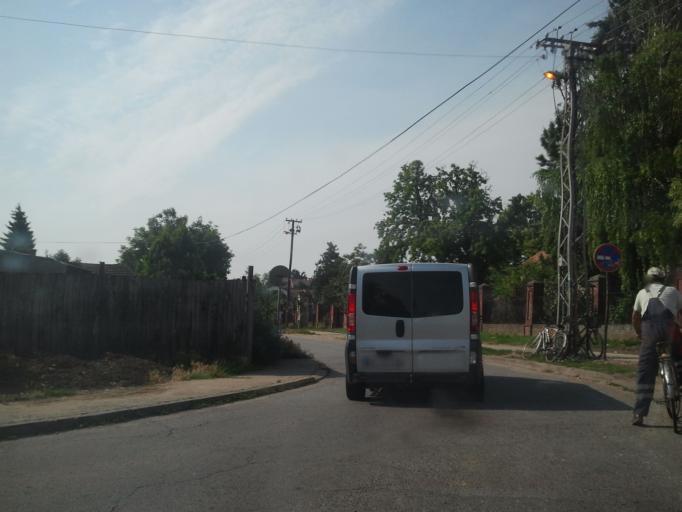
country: RS
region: Autonomna Pokrajina Vojvodina
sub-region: Juznobacki Okrug
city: Petrovaradin
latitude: 45.2359
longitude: 19.8880
